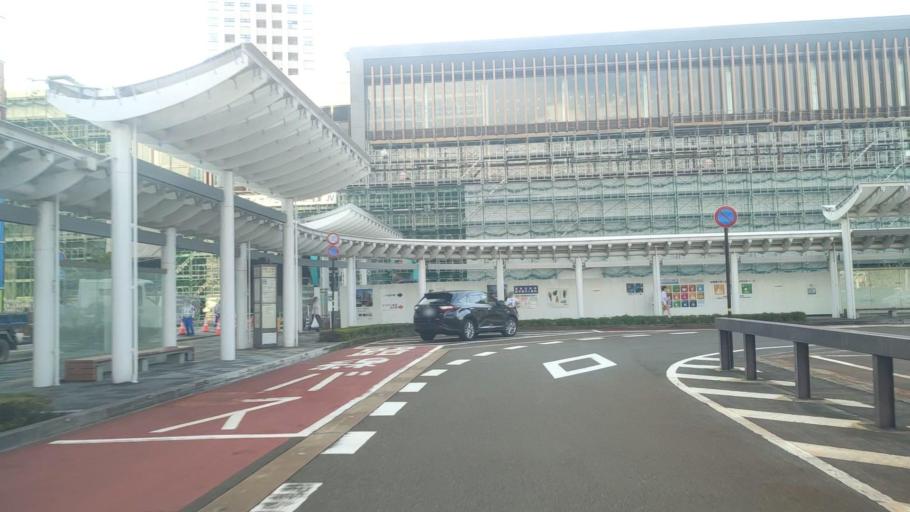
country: JP
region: Fukui
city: Fukui-shi
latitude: 36.0610
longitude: 136.2238
